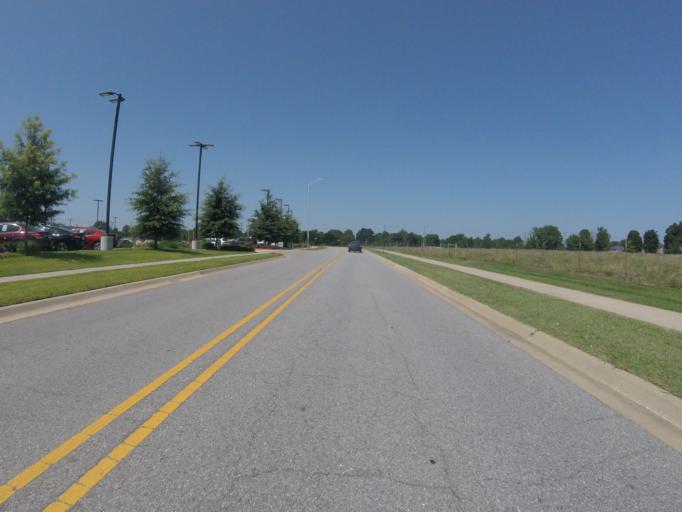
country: US
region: Arkansas
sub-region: Washington County
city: Johnson
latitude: 36.0945
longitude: -94.1917
